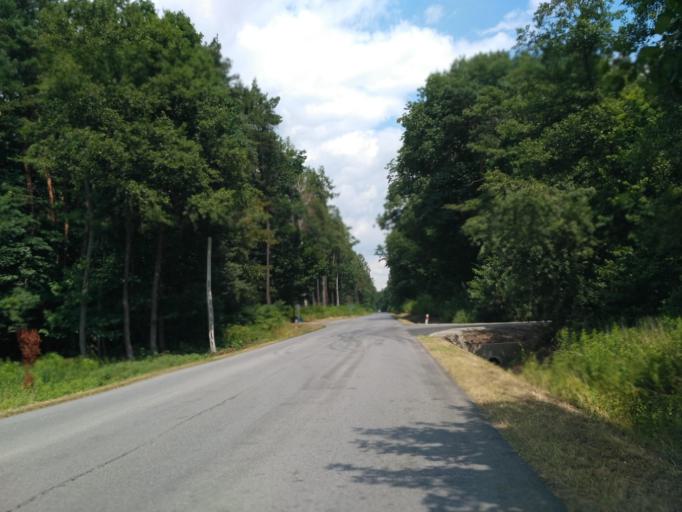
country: PL
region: Subcarpathian Voivodeship
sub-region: Powiat debicki
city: Pilzno
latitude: 50.0203
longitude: 21.2909
